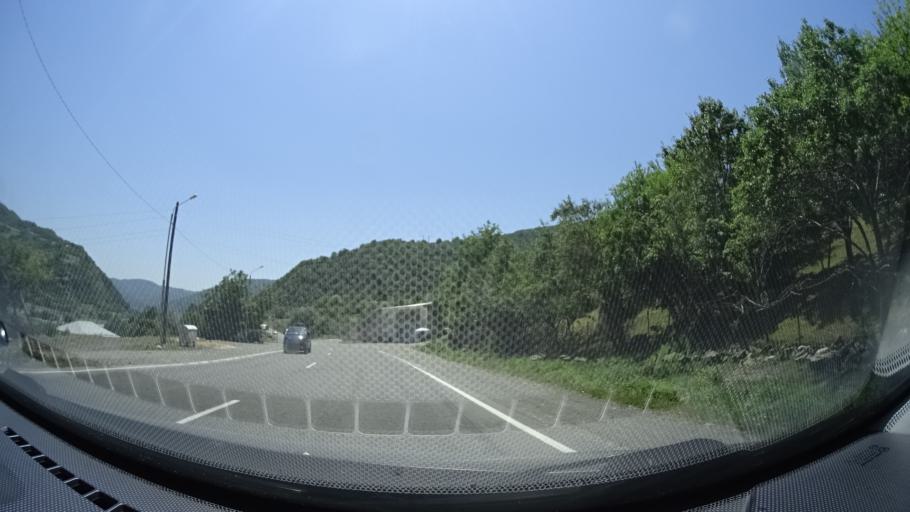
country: GE
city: Zhinvali
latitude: 42.2042
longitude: 44.6740
